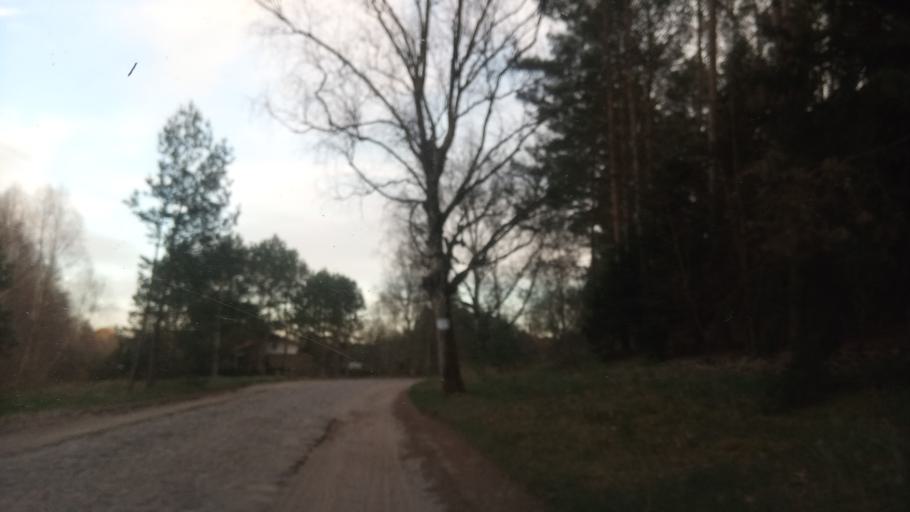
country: PL
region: West Pomeranian Voivodeship
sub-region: Powiat szczecinecki
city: Lubowo
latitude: 53.5556
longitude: 16.3887
